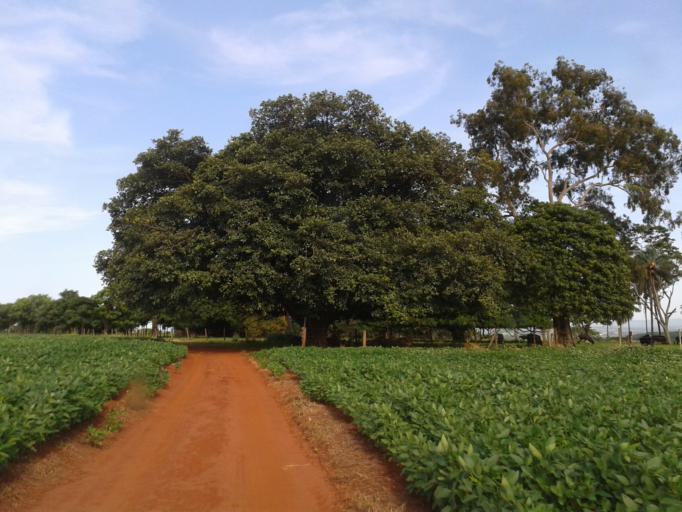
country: BR
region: Minas Gerais
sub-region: Centralina
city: Centralina
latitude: -18.7126
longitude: -49.1903
